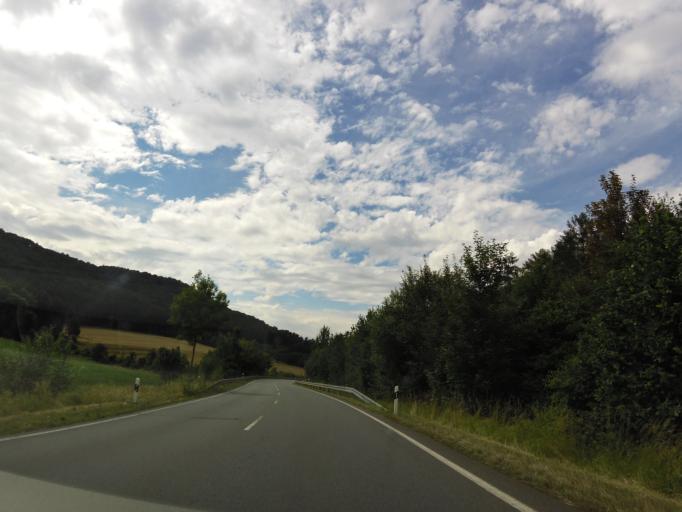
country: DE
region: Lower Saxony
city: Furstenberg
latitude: 51.7060
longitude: 9.3814
